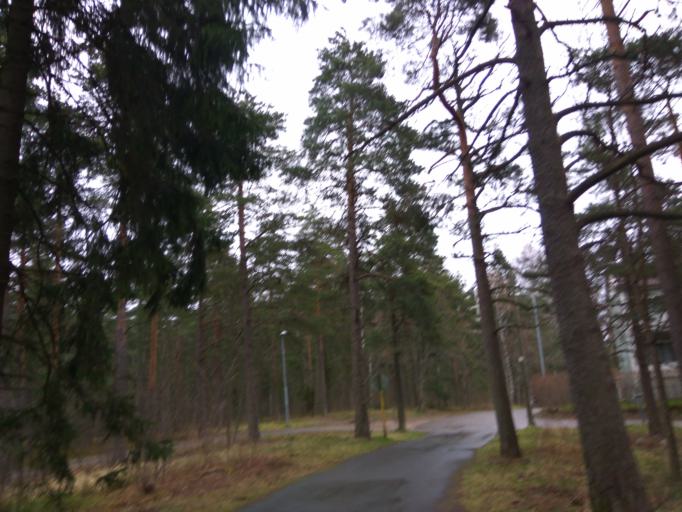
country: FI
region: Uusimaa
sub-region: Helsinki
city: Helsinki
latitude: 60.2218
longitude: 24.9555
